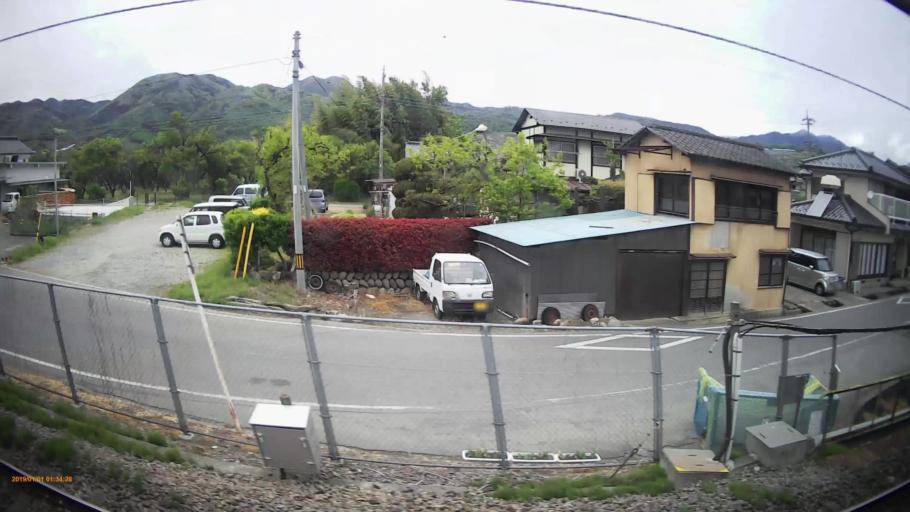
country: JP
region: Yamanashi
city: Isawa
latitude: 35.6843
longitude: 138.6724
